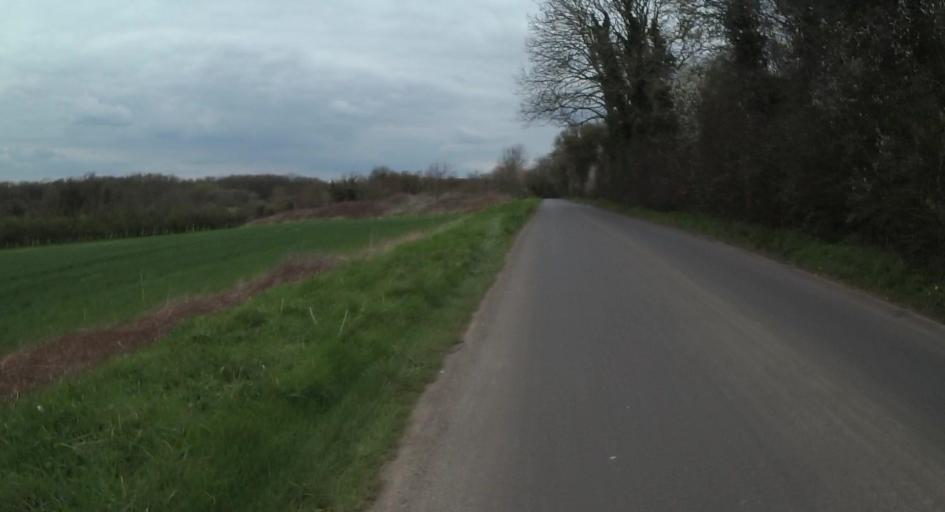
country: GB
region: England
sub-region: Hampshire
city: Odiham
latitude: 51.2436
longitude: -0.9722
